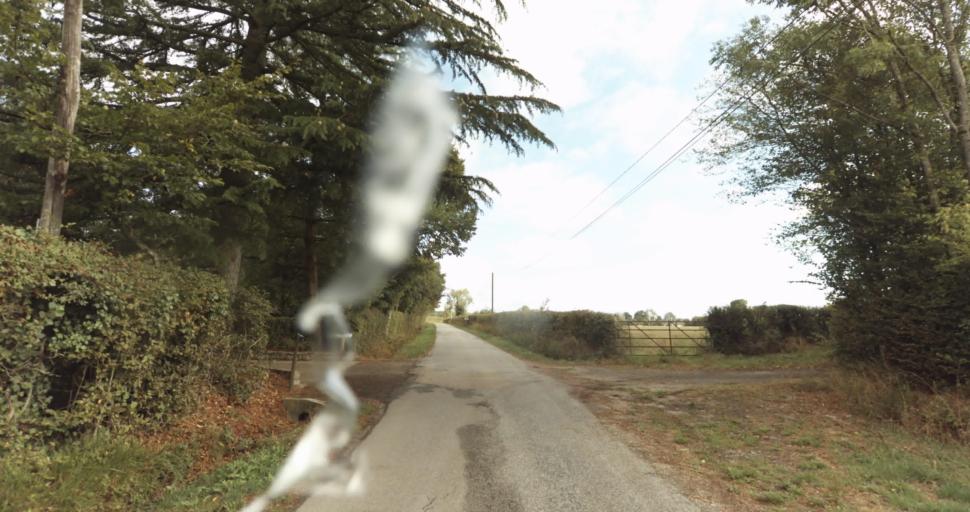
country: FR
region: Lower Normandy
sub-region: Departement de l'Orne
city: Gace
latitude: 48.8558
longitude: 0.3238
